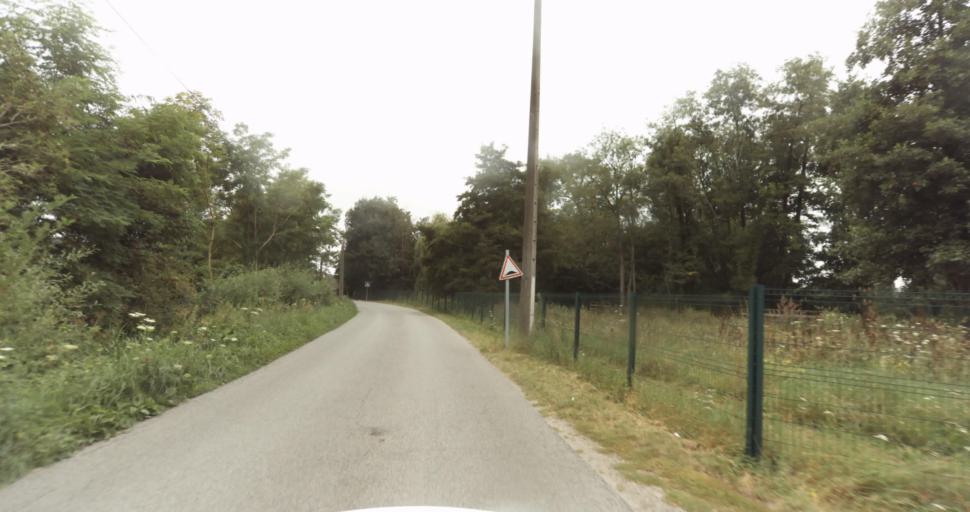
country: FR
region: Haute-Normandie
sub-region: Departement de l'Eure
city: Saint-Germain-sur-Avre
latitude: 48.7620
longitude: 1.2675
